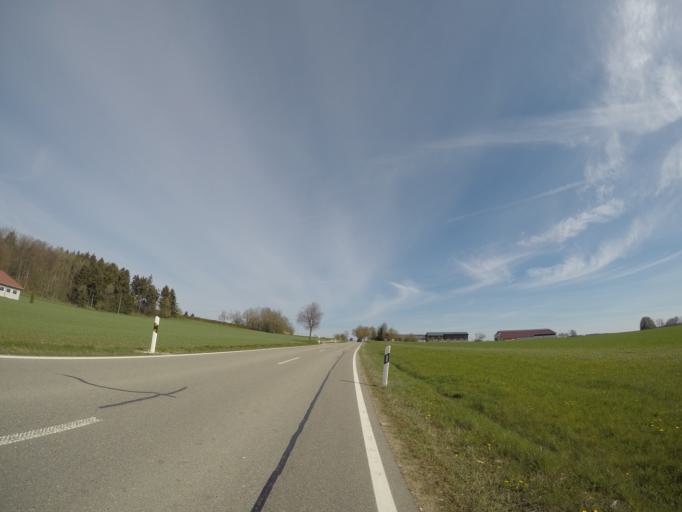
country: DE
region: Baden-Wuerttemberg
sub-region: Tuebingen Region
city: Laichingen
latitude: 48.5072
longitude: 9.6731
